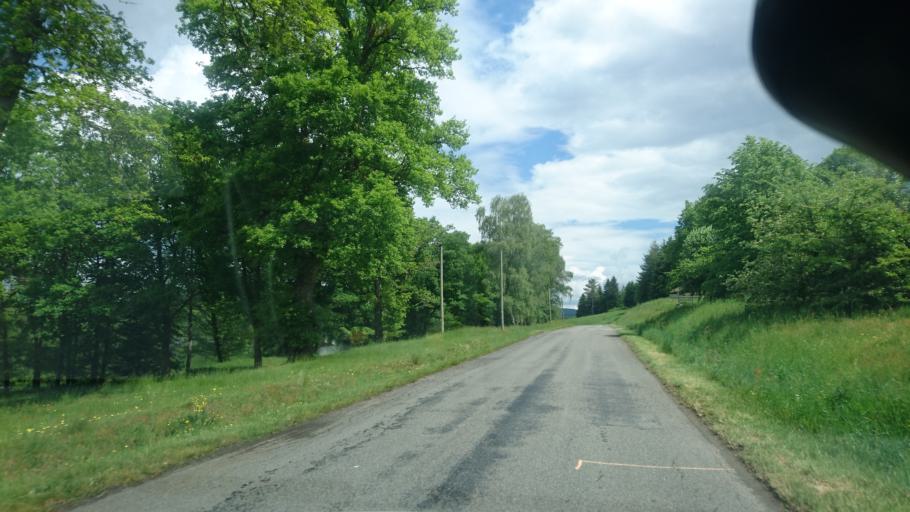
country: FR
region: Limousin
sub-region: Departement de la Haute-Vienne
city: Peyrat-le-Chateau
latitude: 45.7858
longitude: 1.8814
